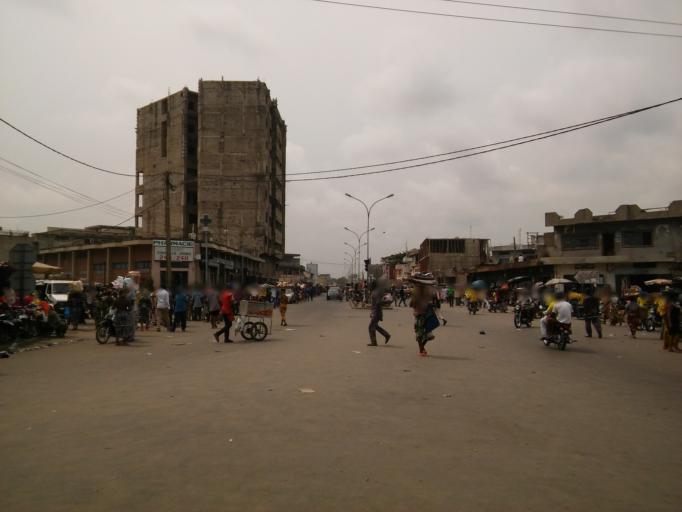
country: BJ
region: Littoral
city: Cotonou
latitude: 6.3696
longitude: 2.4310
